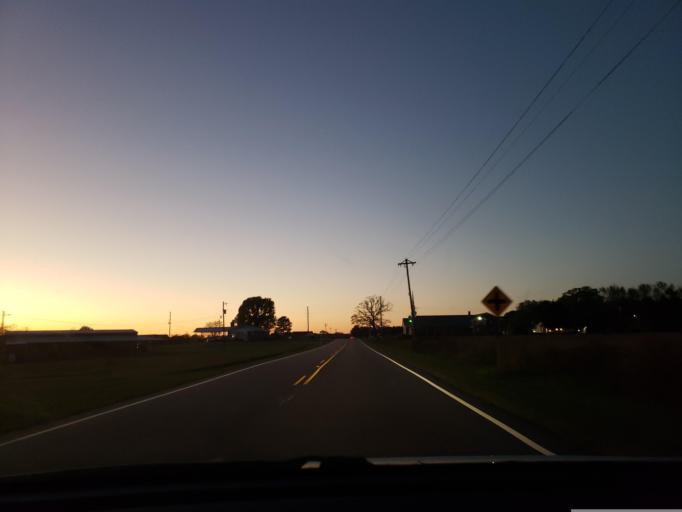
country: US
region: North Carolina
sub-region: Duplin County
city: Kenansville
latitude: 34.9027
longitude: -77.9175
